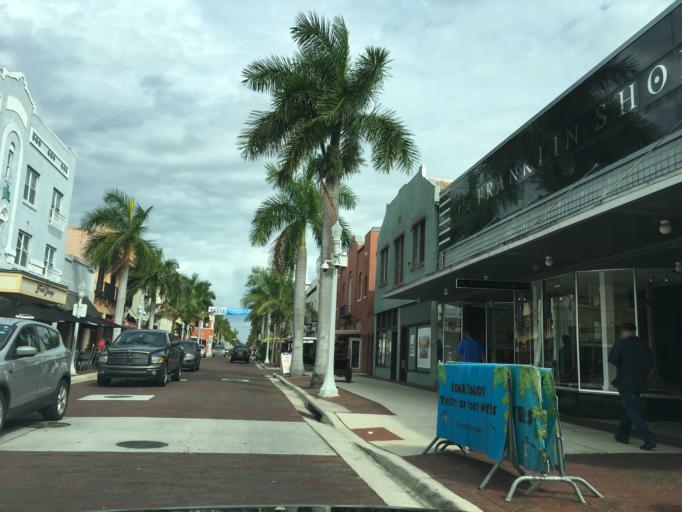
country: US
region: Florida
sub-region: Lee County
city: North Fort Myers
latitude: 26.6439
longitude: -81.8707
